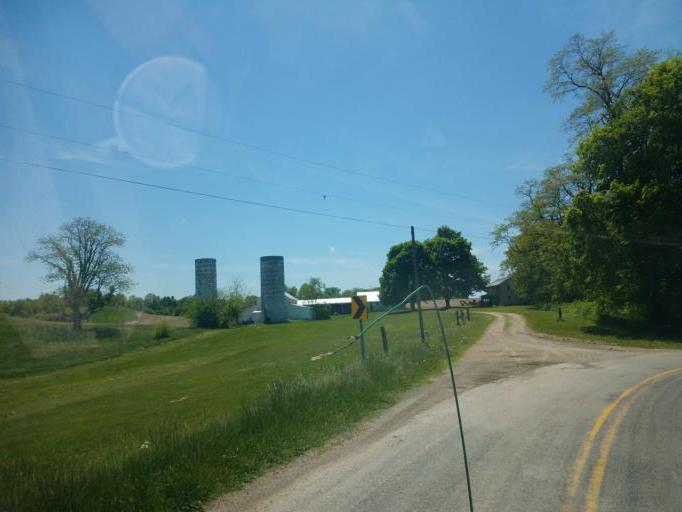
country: US
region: Ohio
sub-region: Ashland County
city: Ashland
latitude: 40.9667
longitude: -82.3813
